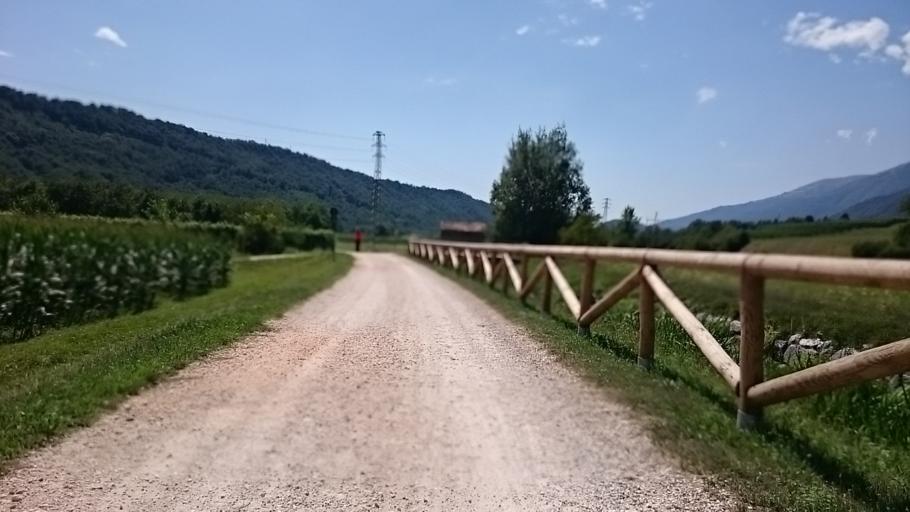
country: IT
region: Veneto
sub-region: Provincia di Treviso
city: Cison di Valmarino
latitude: 45.9684
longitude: 12.1602
